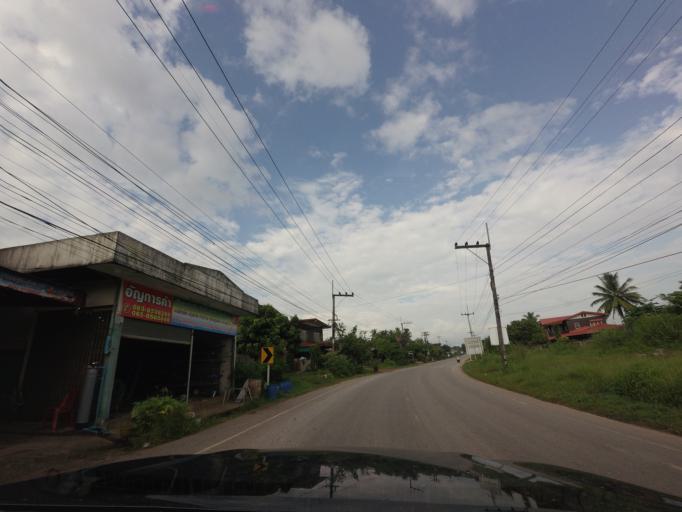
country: TH
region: Nong Khai
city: Pho Tak
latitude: 17.7794
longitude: 102.3908
